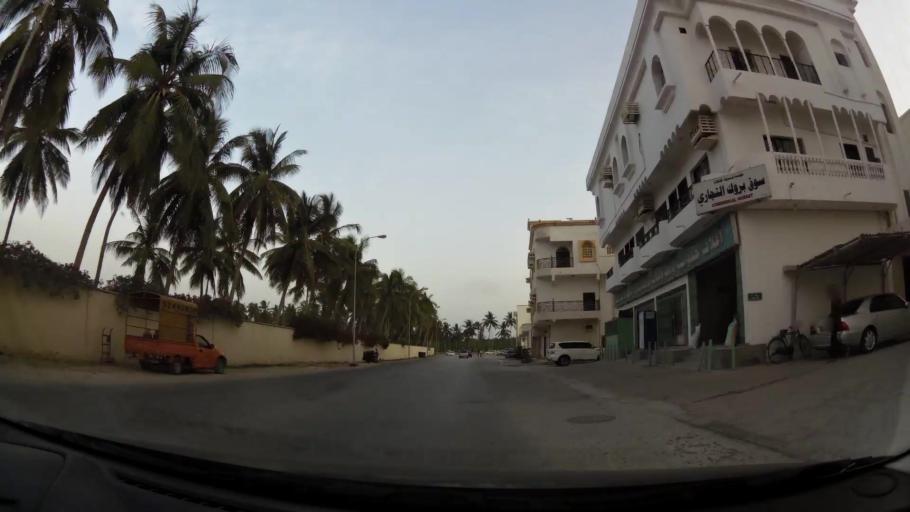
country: OM
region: Zufar
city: Salalah
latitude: 17.0207
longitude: 54.1289
